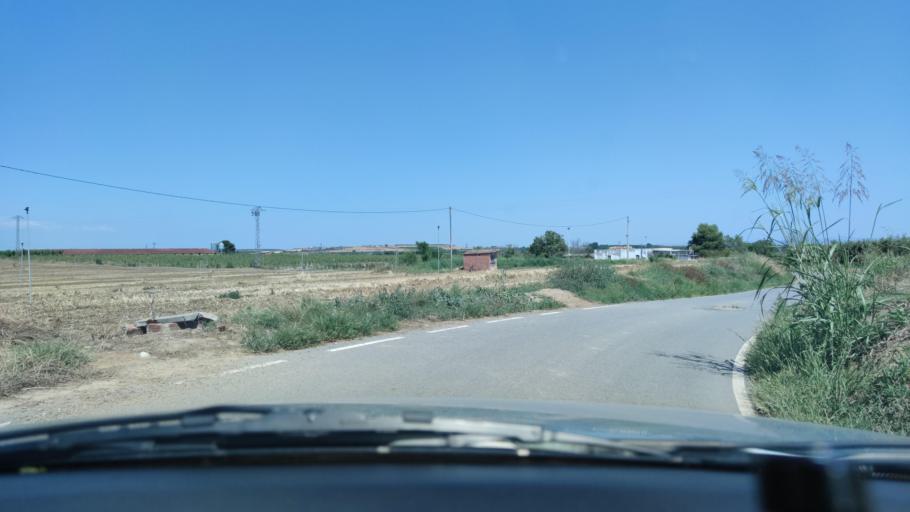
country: ES
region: Catalonia
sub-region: Provincia de Lleida
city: Torrefarrera
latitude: 41.6771
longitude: 0.6416
